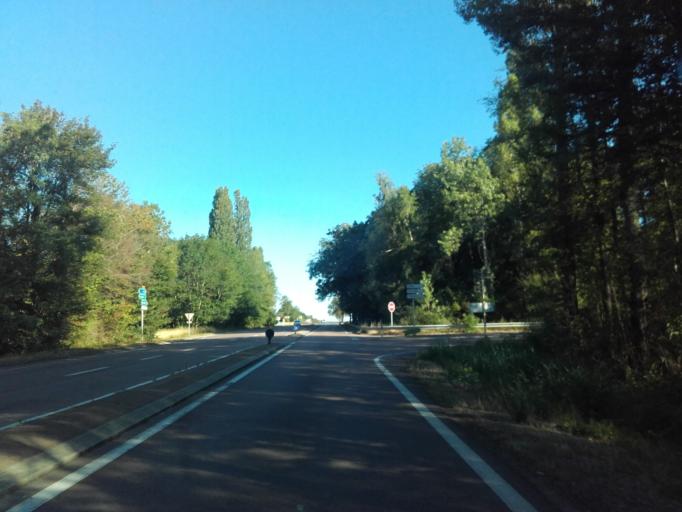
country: FR
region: Bourgogne
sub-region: Departement de Saone-et-Loire
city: Fontaines
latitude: 46.8801
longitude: 4.7798
